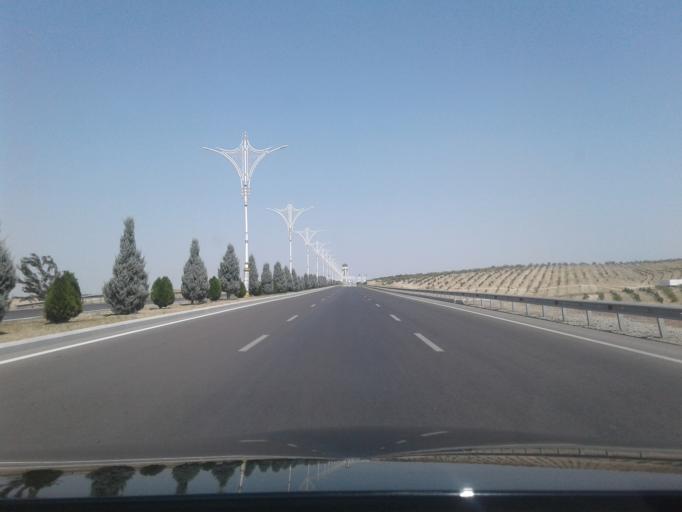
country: TM
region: Ahal
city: Ashgabat
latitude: 37.8783
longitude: 58.4104
